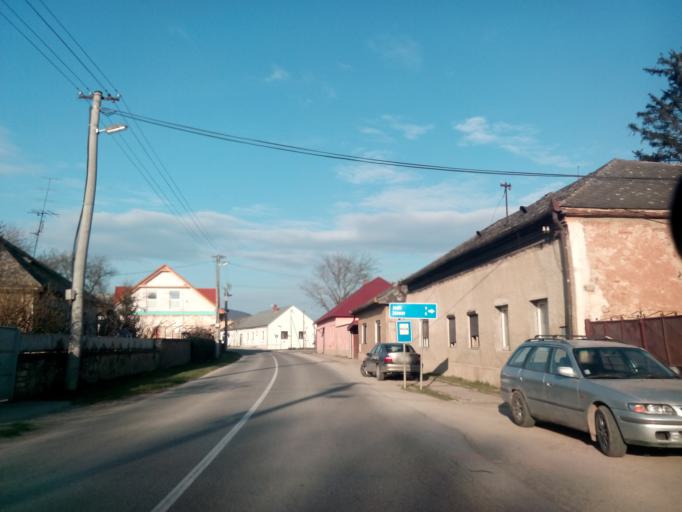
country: SK
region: Kosicky
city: Medzev
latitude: 48.5980
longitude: 20.8738
